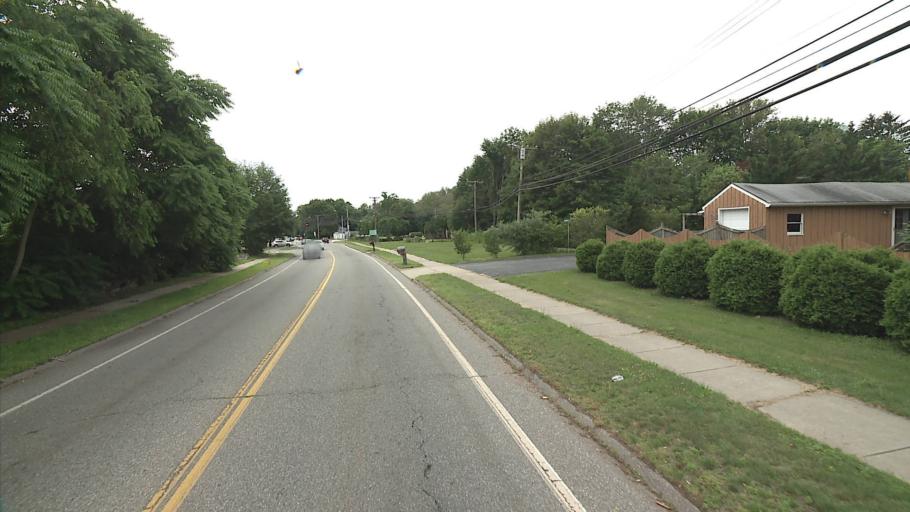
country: US
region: Connecticut
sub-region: New London County
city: Long Hill
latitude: 41.3843
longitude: -72.0278
